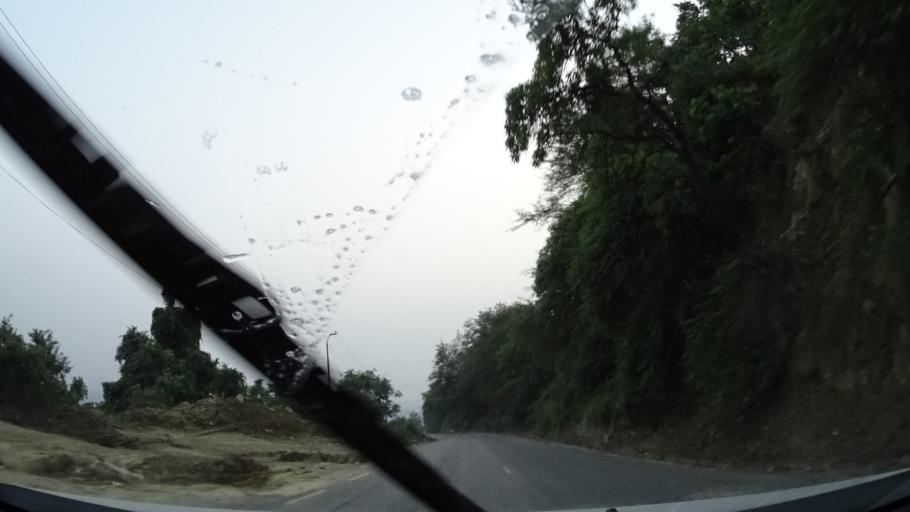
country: IN
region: Uttar Pradesh
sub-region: Maharajganj
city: Nichlaul
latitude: 27.5522
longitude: 83.8125
